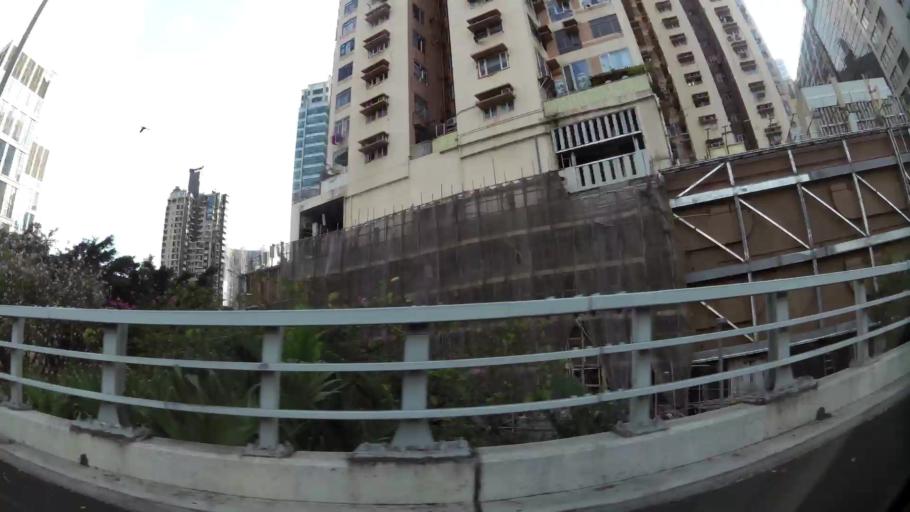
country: HK
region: Wanchai
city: Wan Chai
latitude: 22.2799
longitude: 114.1874
